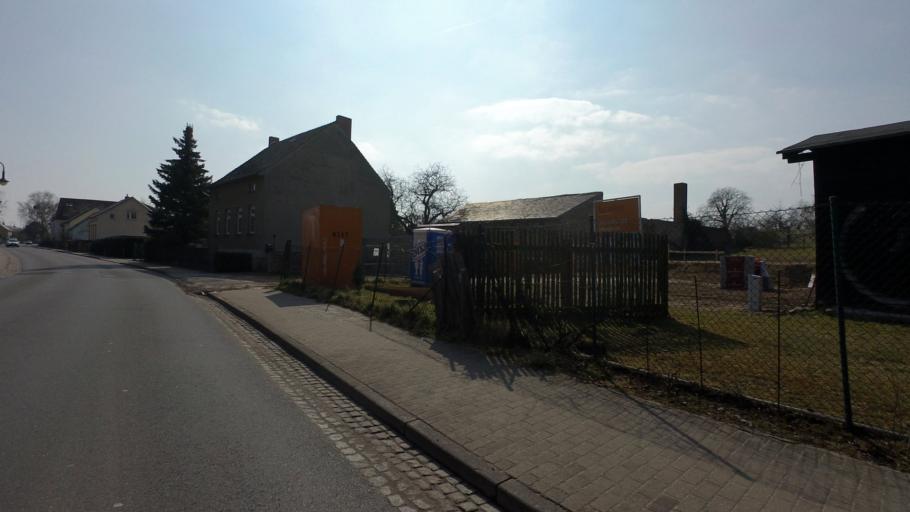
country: DE
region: Brandenburg
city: Werder
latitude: 52.3684
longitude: 12.9379
